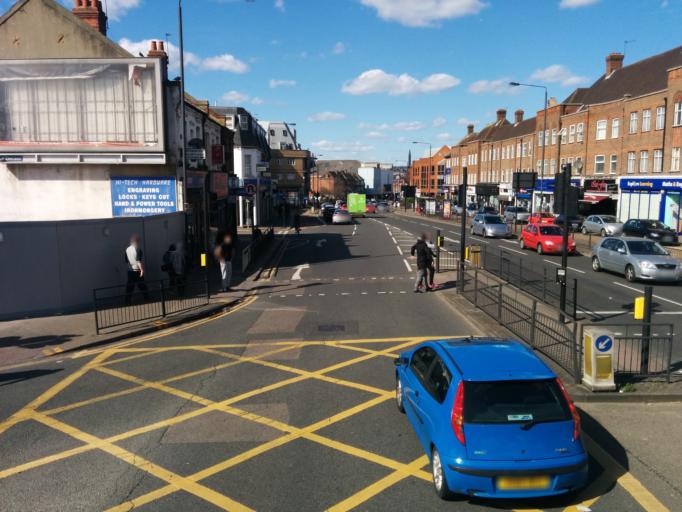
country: GB
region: England
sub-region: Greater London
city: Harrow
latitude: 51.5839
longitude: -0.3319
